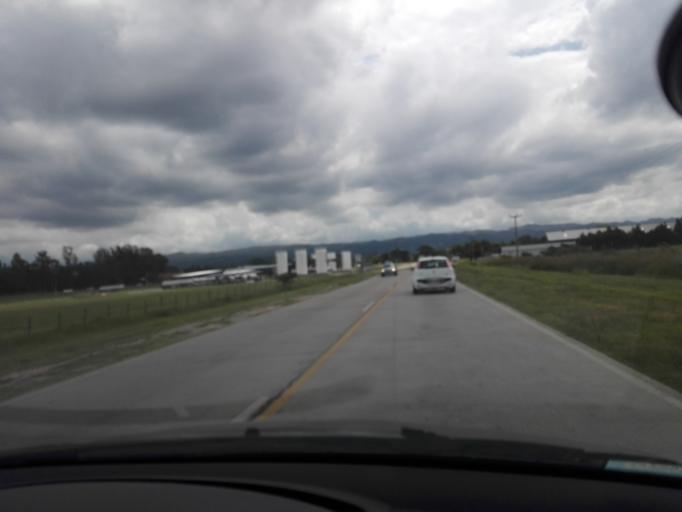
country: AR
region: Cordoba
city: Alta Gracia
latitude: -31.6347
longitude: -64.4315
